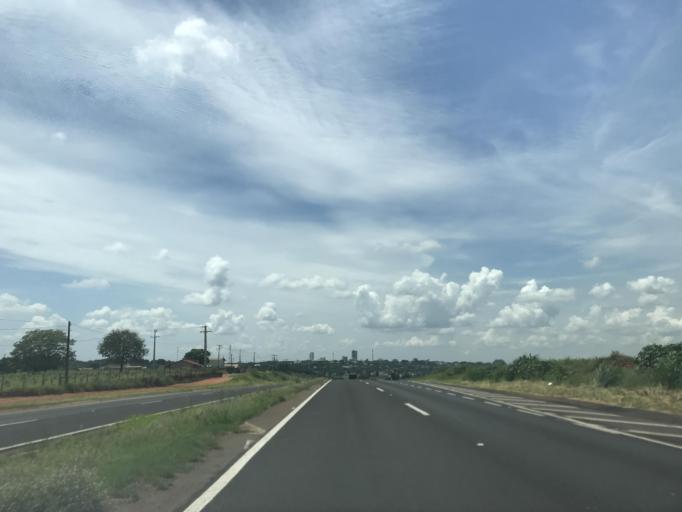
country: BR
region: Parana
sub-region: Alto Parana
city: Alto Parana
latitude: -23.1783
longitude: -52.2257
